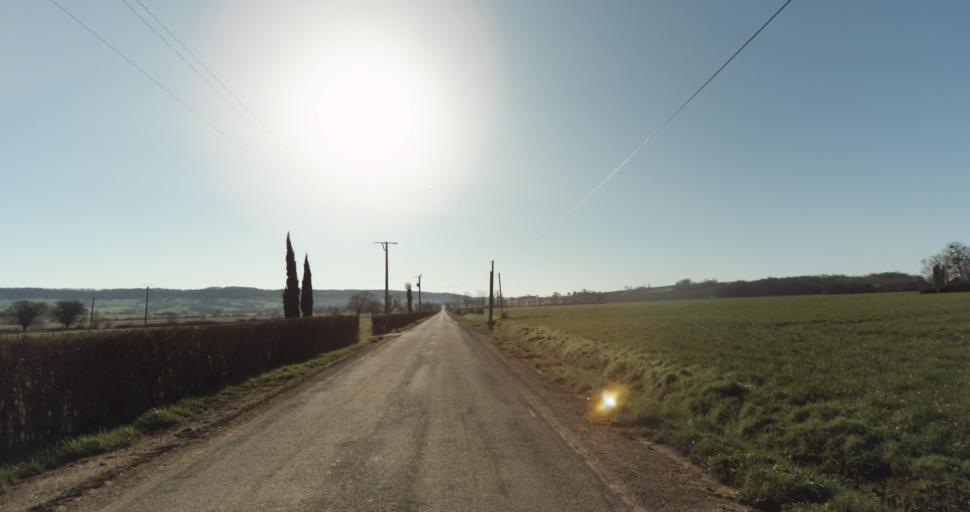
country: FR
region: Lower Normandy
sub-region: Departement du Calvados
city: Saint-Pierre-sur-Dives
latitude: 48.9967
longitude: 0.0107
